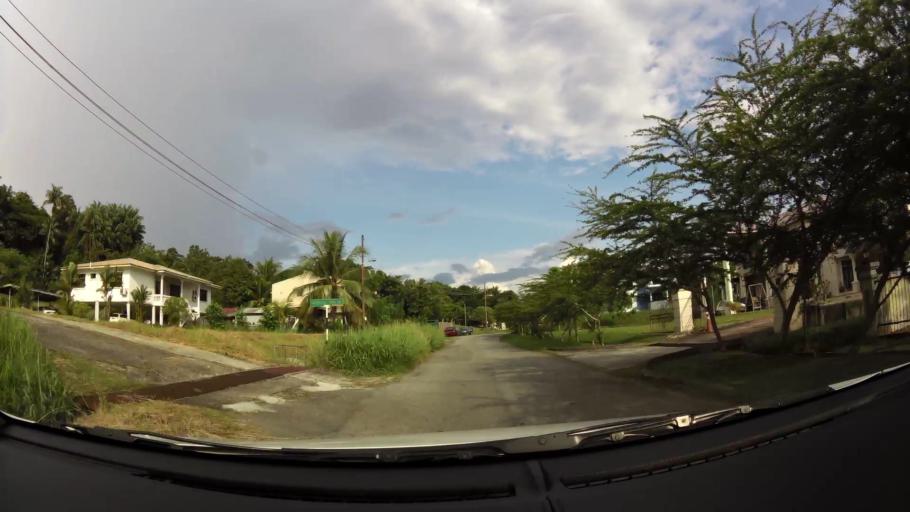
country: BN
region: Brunei and Muara
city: Bandar Seri Begawan
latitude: 4.9692
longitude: 114.9801
